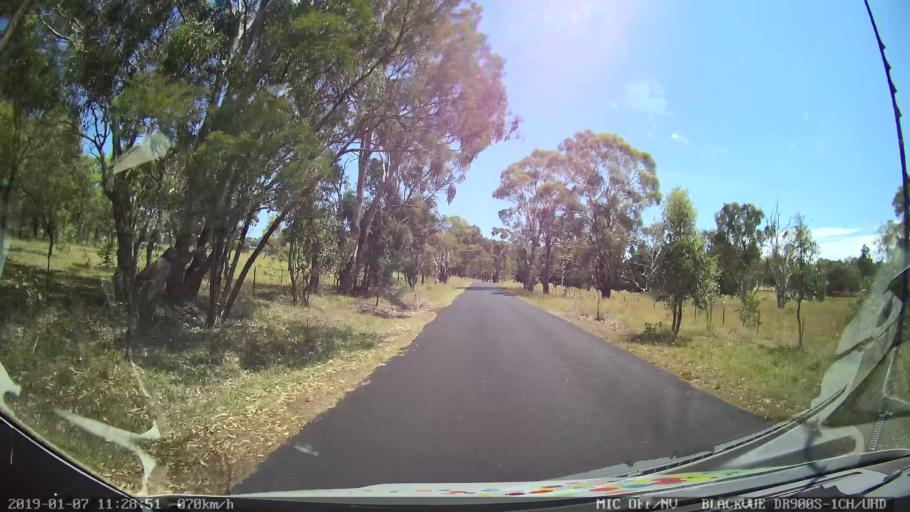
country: AU
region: New South Wales
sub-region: Armidale Dumaresq
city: Armidale
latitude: -30.4444
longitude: 151.5649
